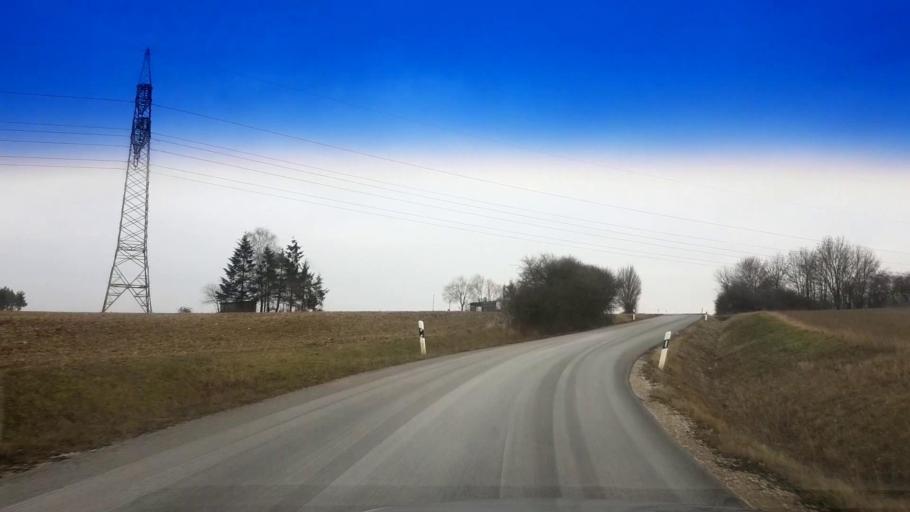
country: DE
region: Bavaria
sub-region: Upper Franconia
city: Hallerndorf
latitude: 49.7853
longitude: 10.9611
